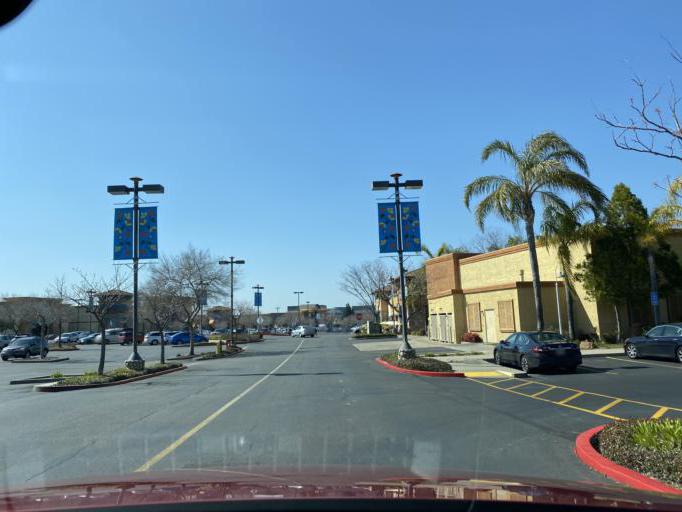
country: US
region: California
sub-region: El Dorado County
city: El Dorado Hills
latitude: 38.6451
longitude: -121.1208
